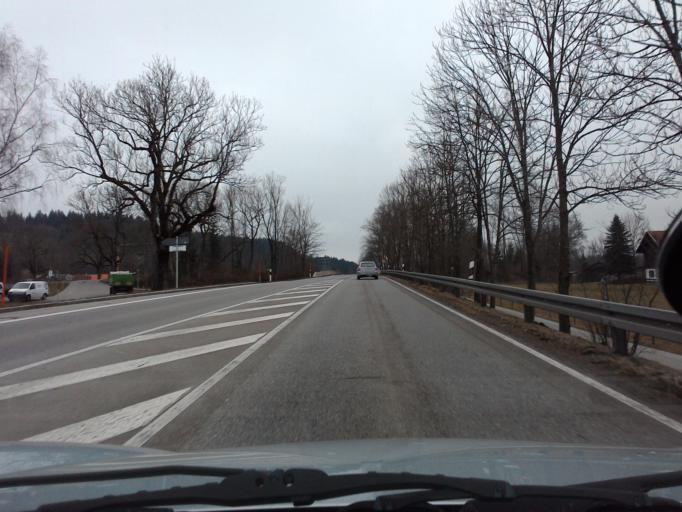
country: DE
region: Bavaria
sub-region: Swabia
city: Bolsterlang
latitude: 47.4697
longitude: 10.2680
